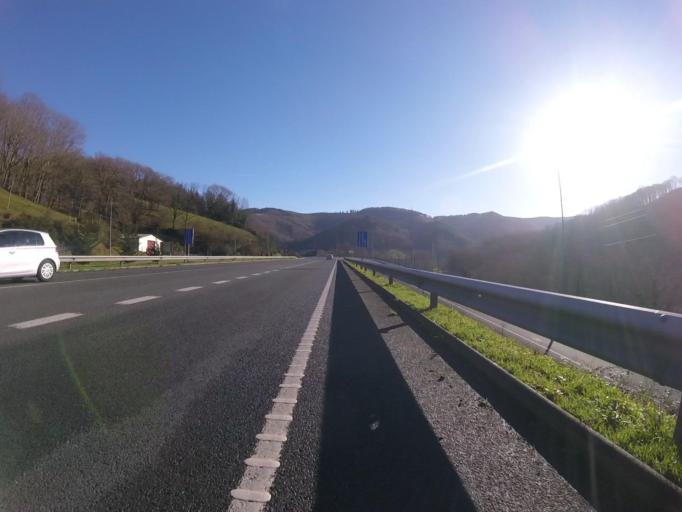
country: ES
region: Navarre
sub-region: Provincia de Navarra
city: Bera
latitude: 43.2809
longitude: -1.7117
